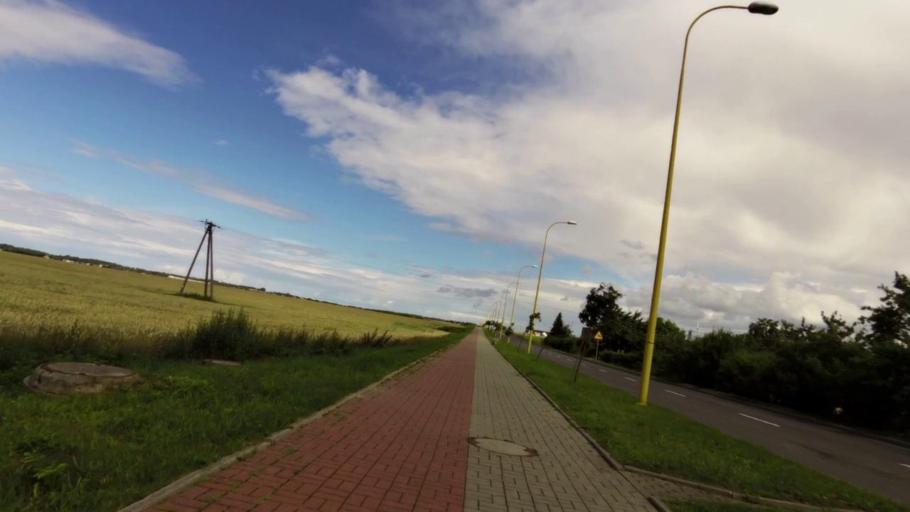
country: PL
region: West Pomeranian Voivodeship
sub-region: Powiat slawienski
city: Darlowo
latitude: 54.4319
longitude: 16.4125
